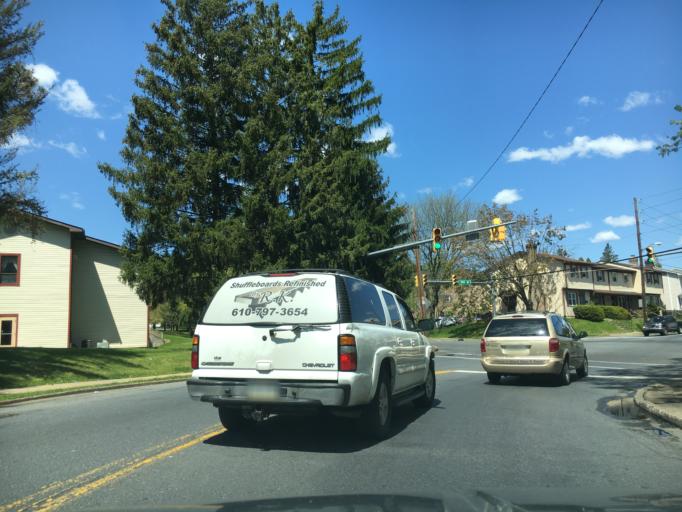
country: US
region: Pennsylvania
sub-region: Lehigh County
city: Allentown
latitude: 40.6114
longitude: -75.4951
